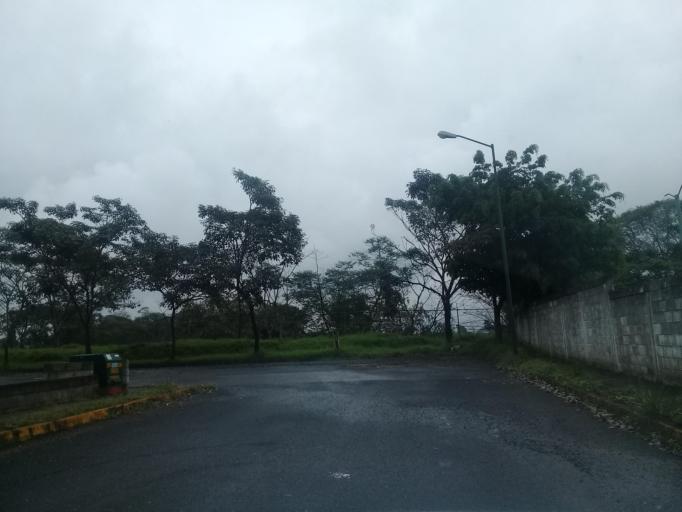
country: MX
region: Veracruz
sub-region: Amatlan de los Reyes
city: Trapiche Viejo
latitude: 18.8373
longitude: -96.9504
